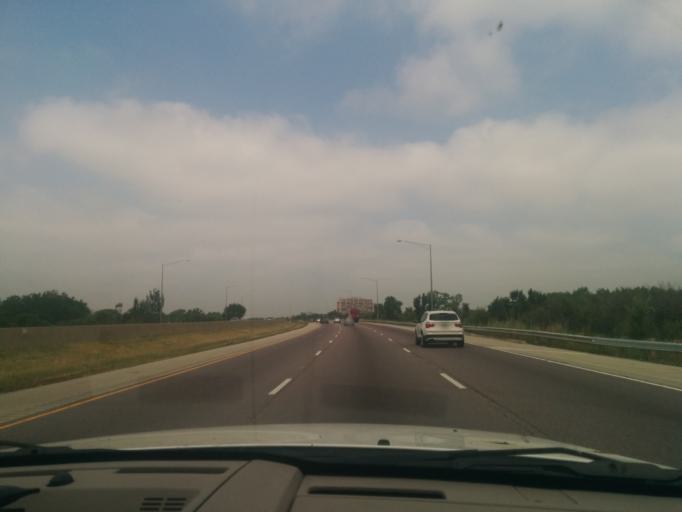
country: US
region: Illinois
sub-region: DuPage County
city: Addison
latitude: 41.9409
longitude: -87.9859
